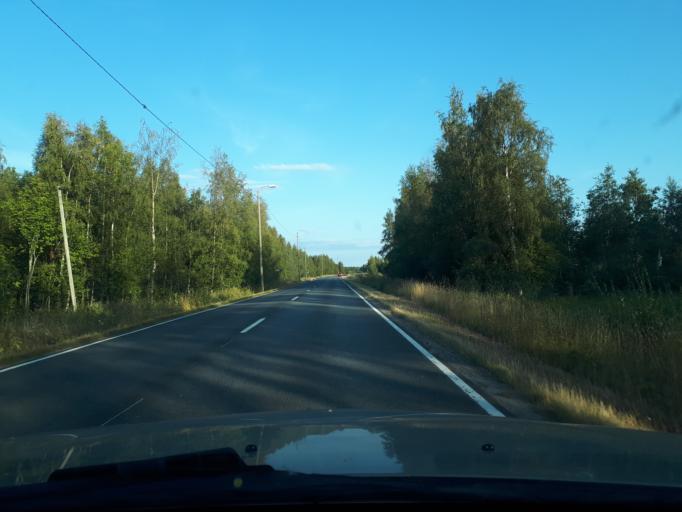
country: FI
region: Northern Ostrobothnia
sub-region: Oulu
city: Oulunsalo
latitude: 64.9843
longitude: 25.2664
